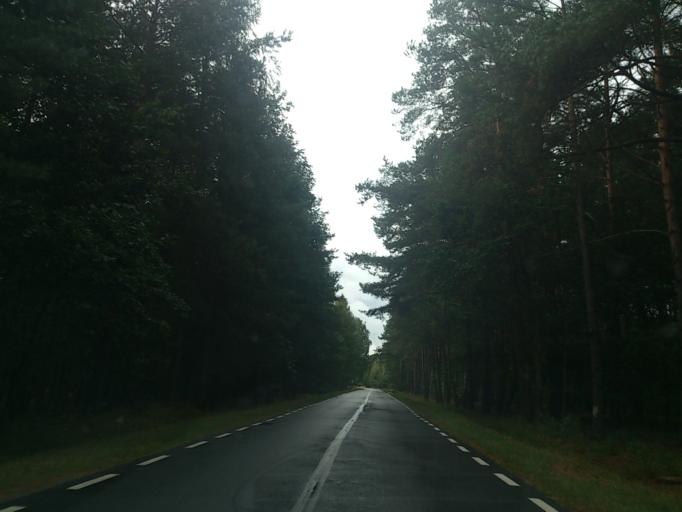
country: PL
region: Greater Poland Voivodeship
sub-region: Powiat poznanski
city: Pobiedziska
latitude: 52.5157
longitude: 17.1940
